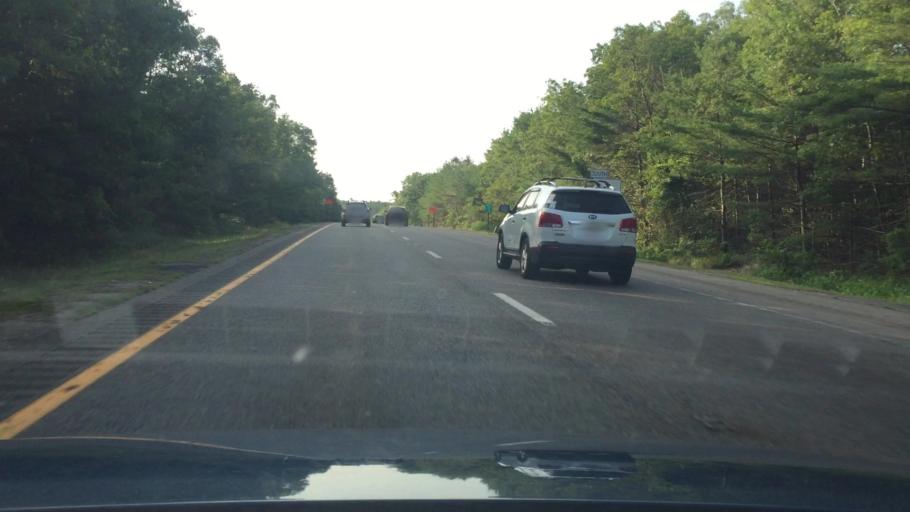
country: US
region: Massachusetts
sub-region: Plymouth County
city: North Pembroke
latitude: 42.1044
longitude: -70.7615
